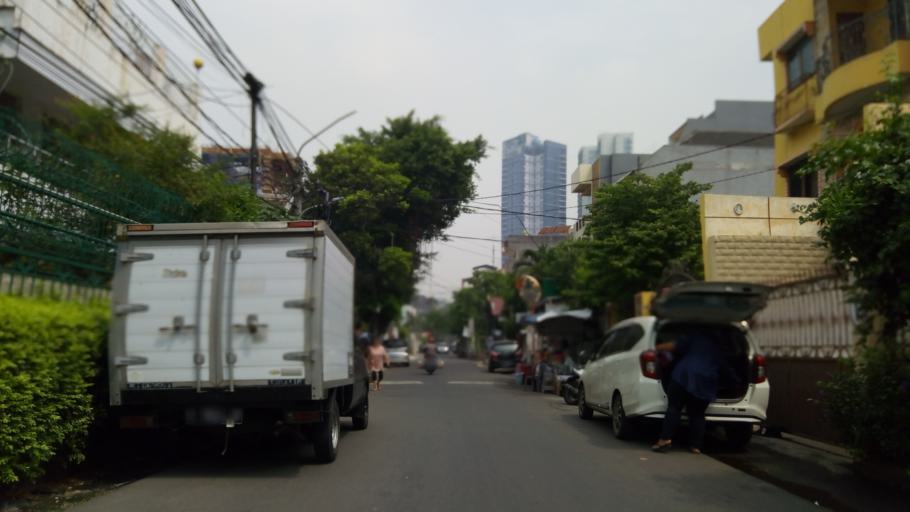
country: ID
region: Jakarta Raya
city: Jakarta
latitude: -6.1619
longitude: 106.8364
